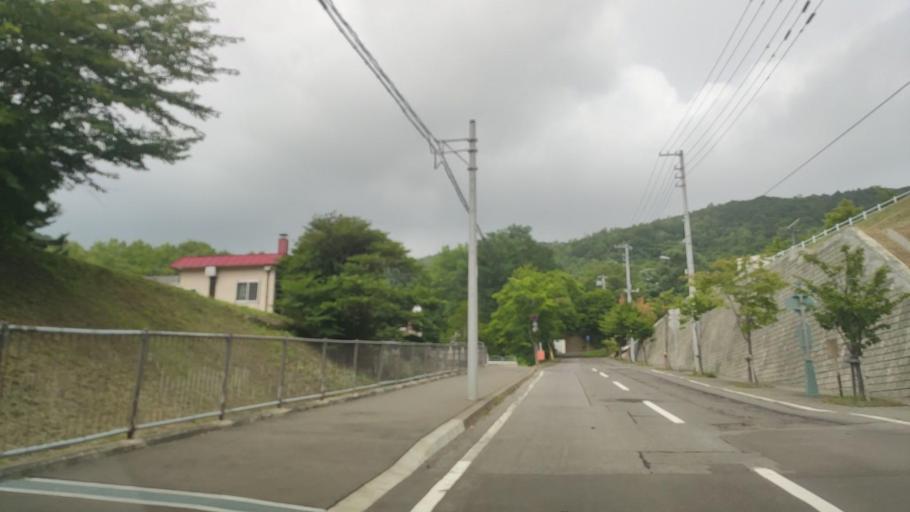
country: JP
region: Hokkaido
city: Otaru
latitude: 43.1917
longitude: 140.9804
